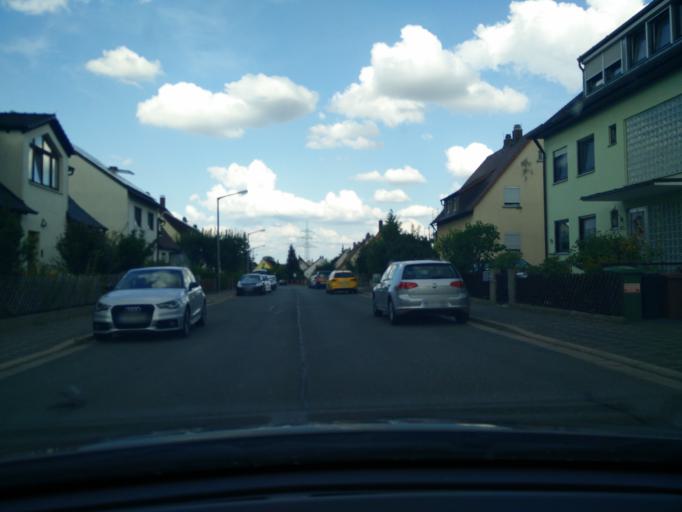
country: DE
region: Bavaria
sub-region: Regierungsbezirk Mittelfranken
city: Stein
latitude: 49.3938
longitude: 10.9959
